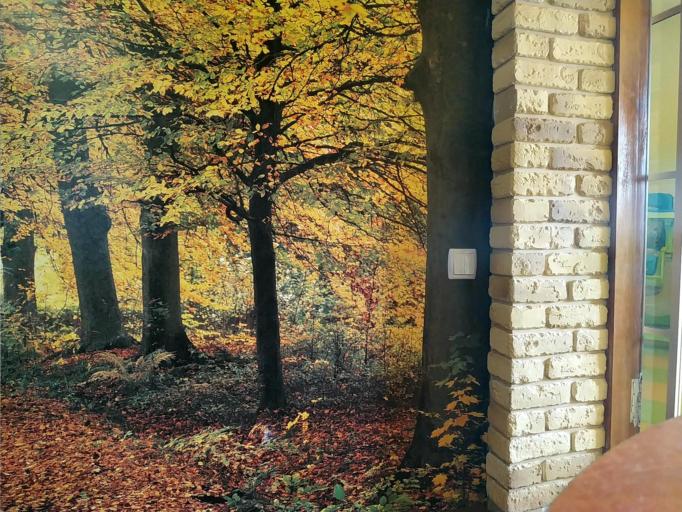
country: RU
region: Smolensk
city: Katyn'
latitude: 54.8790
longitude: 31.8085
